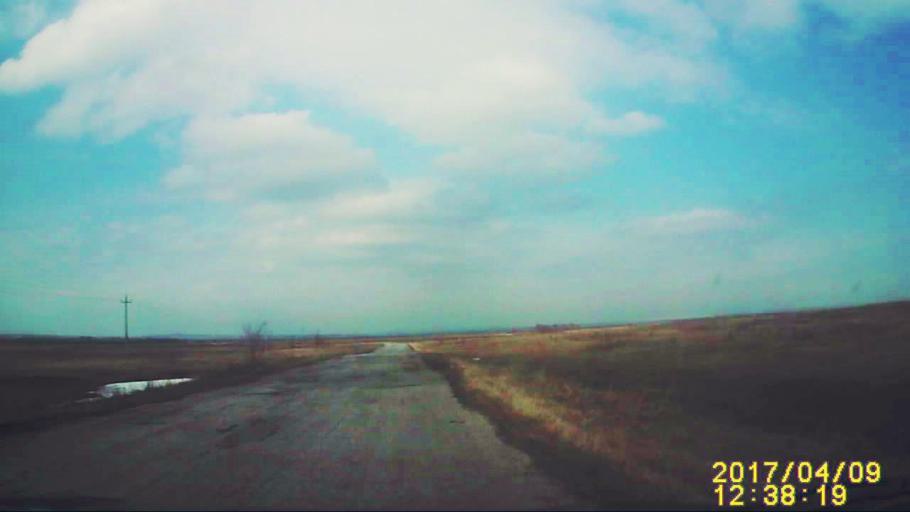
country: RU
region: Ulyanovsk
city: Ignatovka
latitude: 53.9942
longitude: 47.9665
